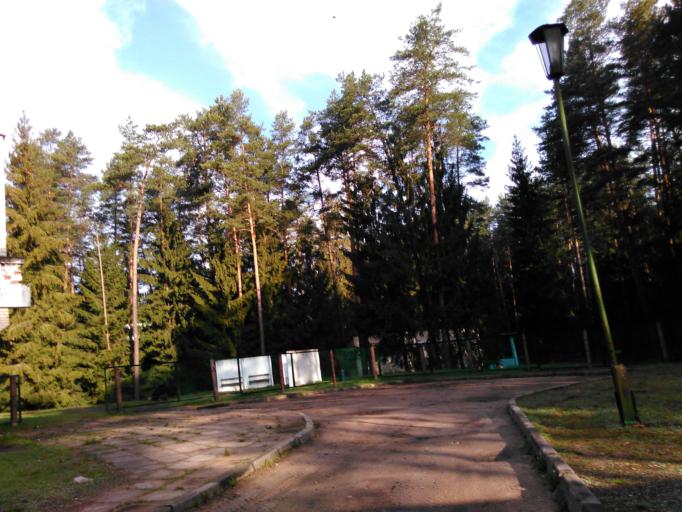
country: BY
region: Minsk
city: Rakaw
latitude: 53.9703
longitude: 27.0173
